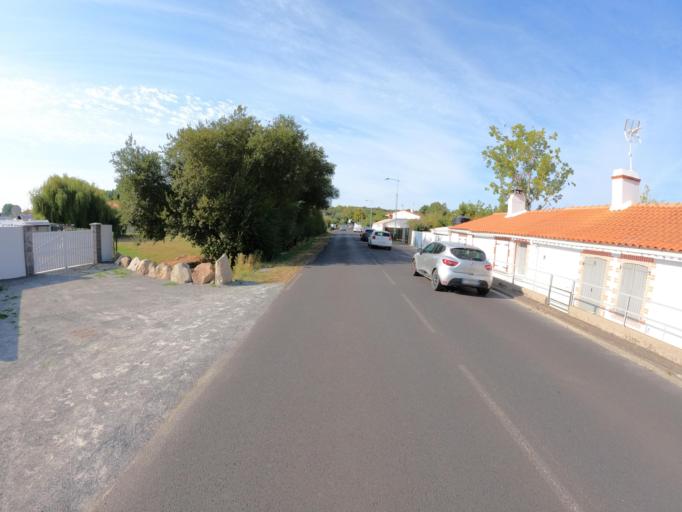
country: FR
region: Pays de la Loire
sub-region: Departement de la Vendee
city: Saint-Jean-de-Monts
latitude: 46.7984
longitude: -2.0686
